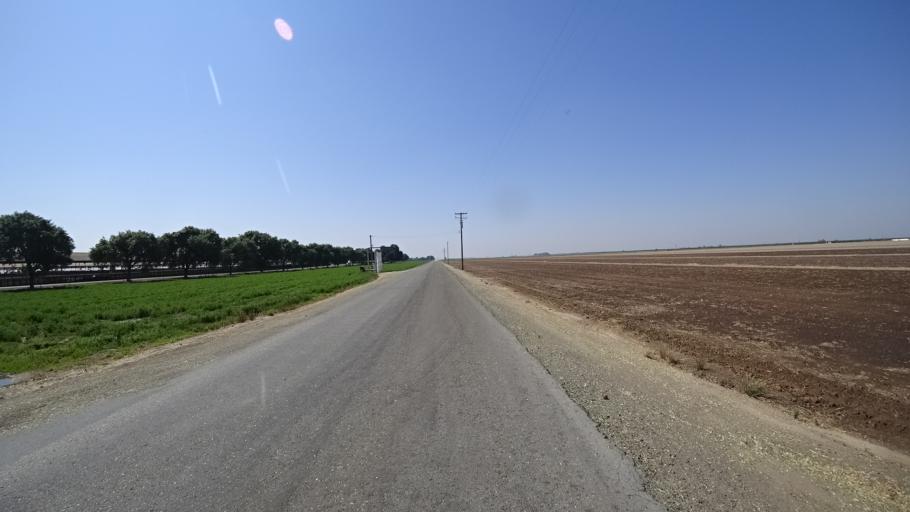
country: US
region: California
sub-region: Tulare County
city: London
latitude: 36.3991
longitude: -119.5290
